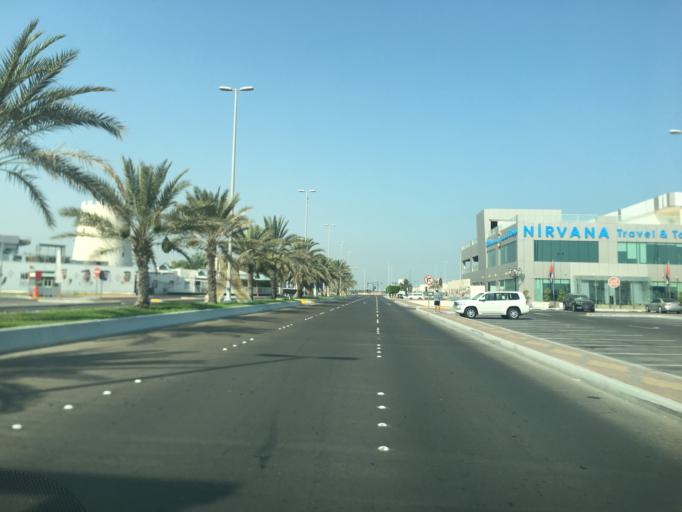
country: AE
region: Abu Dhabi
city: Abu Dhabi
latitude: 24.4734
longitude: 54.3252
